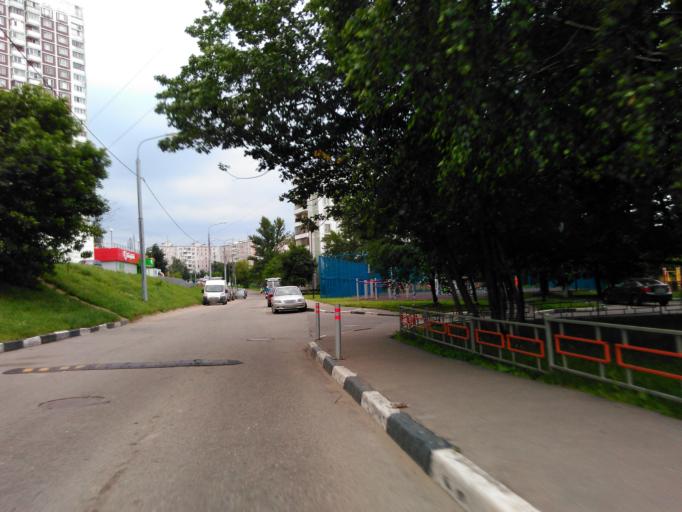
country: RU
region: Moscow
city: Yasenevo
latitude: 55.6077
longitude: 37.5476
